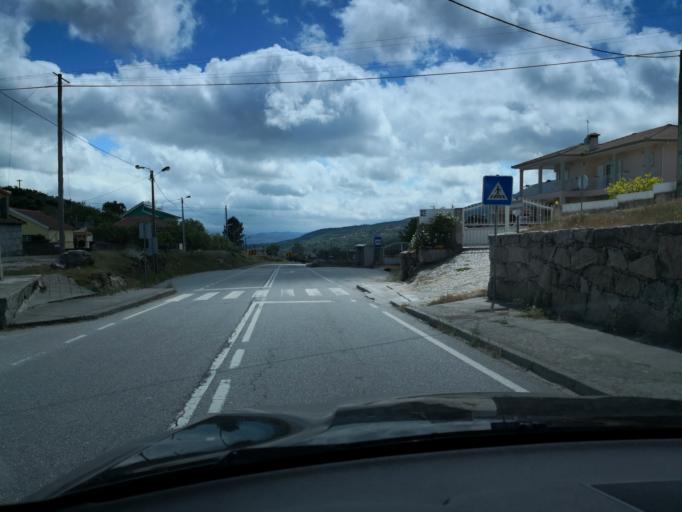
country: PT
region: Vila Real
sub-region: Vila Real
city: Vila Real
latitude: 41.3838
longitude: -7.7078
